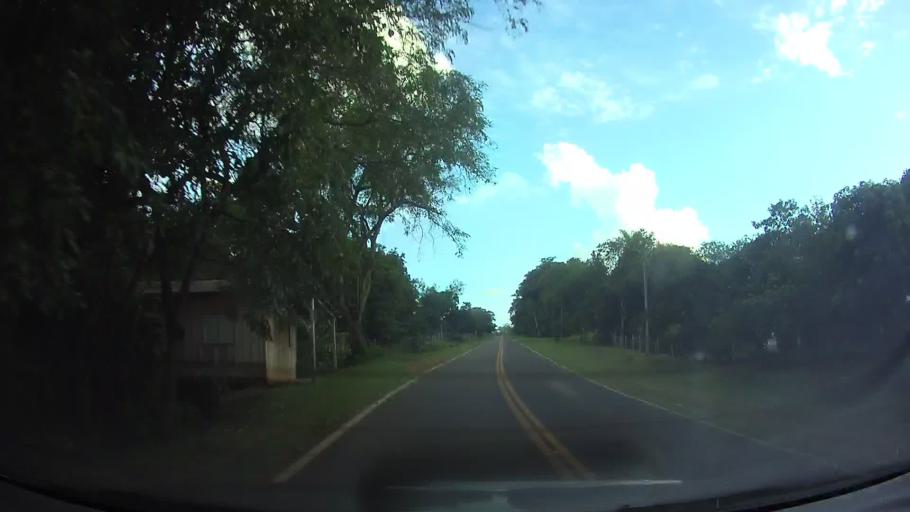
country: PY
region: Paraguari
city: Acahay
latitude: -25.9300
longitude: -57.1061
